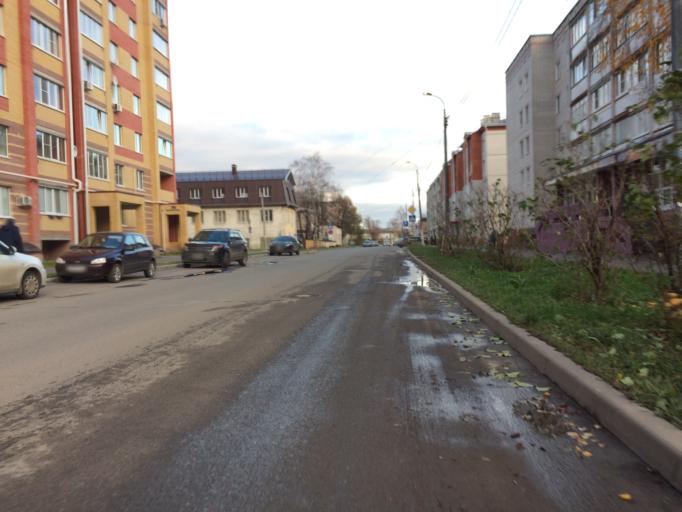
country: RU
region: Mariy-El
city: Yoshkar-Ola
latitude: 56.6473
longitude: 47.8967
